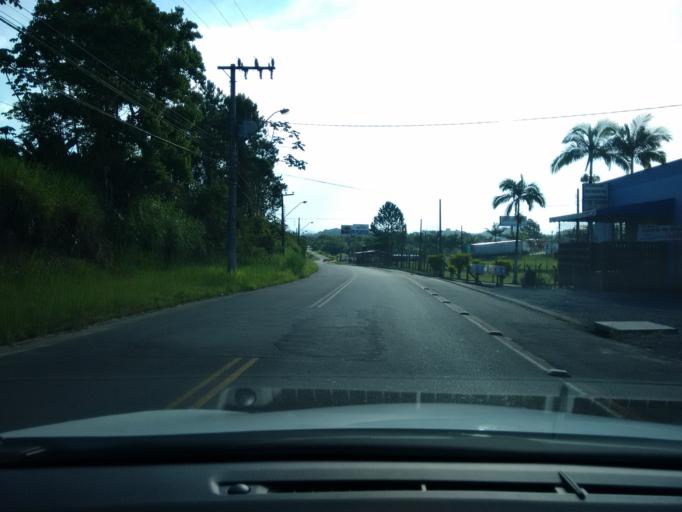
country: BR
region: Santa Catarina
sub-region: Blumenau
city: Blumenau
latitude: -26.8597
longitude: -49.0786
